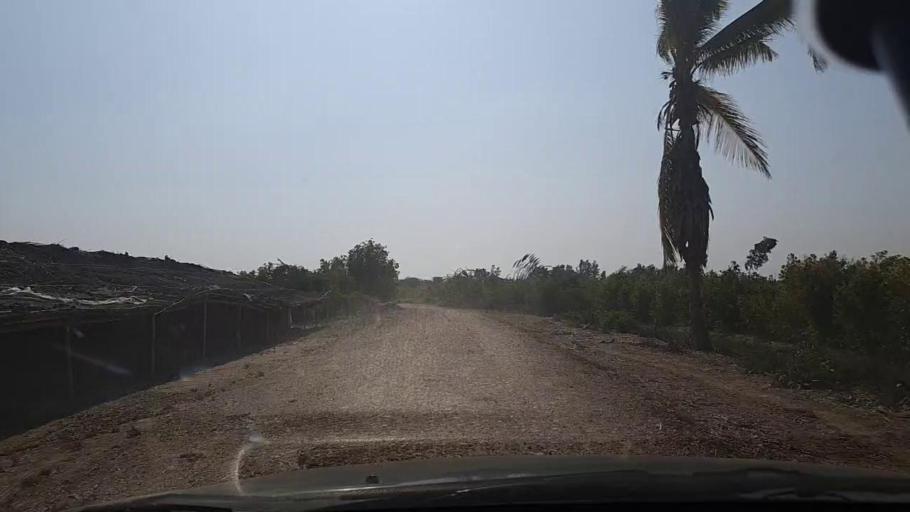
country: PK
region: Sindh
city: Chuhar Jamali
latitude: 24.5194
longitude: 67.8810
